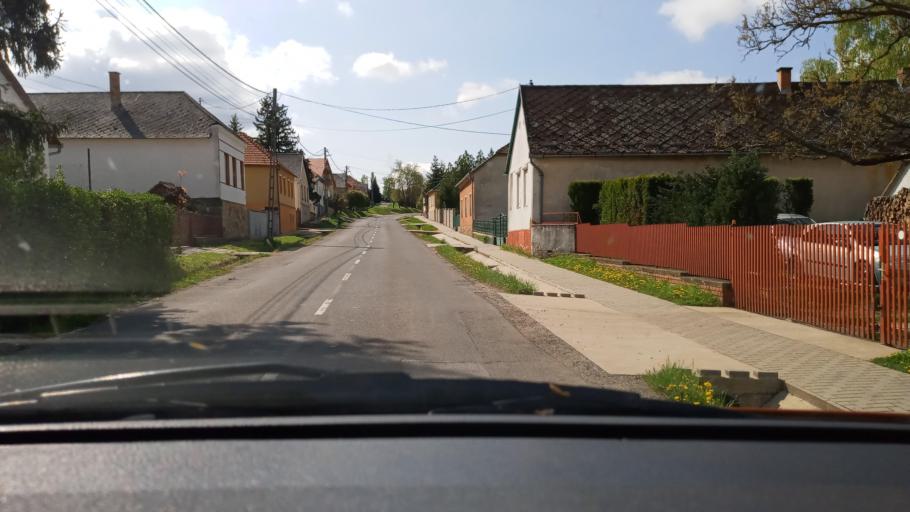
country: HU
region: Baranya
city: Hosszuheteny
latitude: 46.1554
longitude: 18.3554
